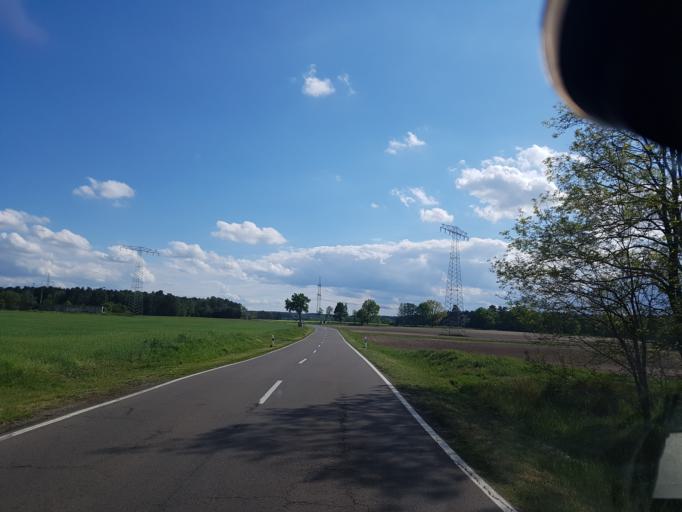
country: DE
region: Brandenburg
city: Drebkau
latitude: 51.6550
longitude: 14.2801
